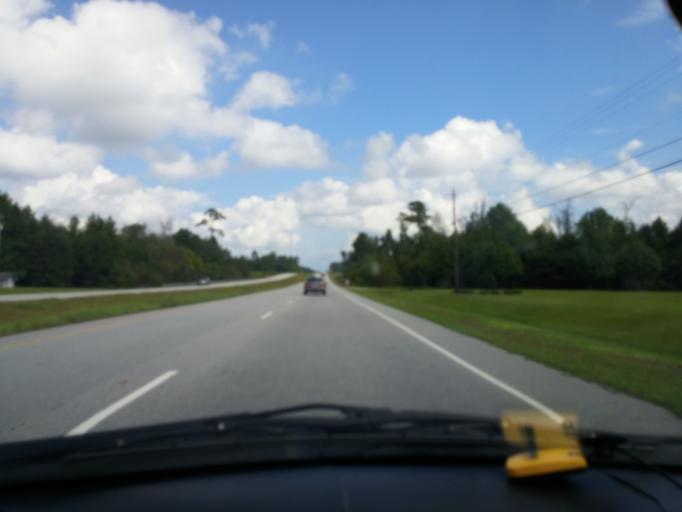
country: US
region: North Carolina
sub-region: Duplin County
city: Beulaville
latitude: 35.1049
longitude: -77.7213
